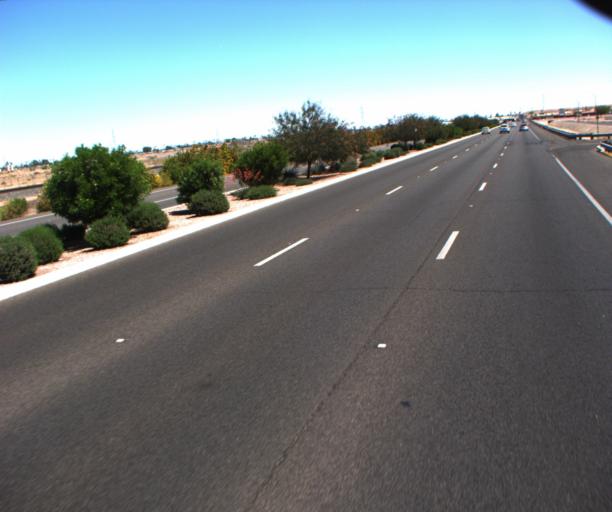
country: US
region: Arizona
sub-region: Maricopa County
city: El Mirage
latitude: 33.6135
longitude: -112.3181
